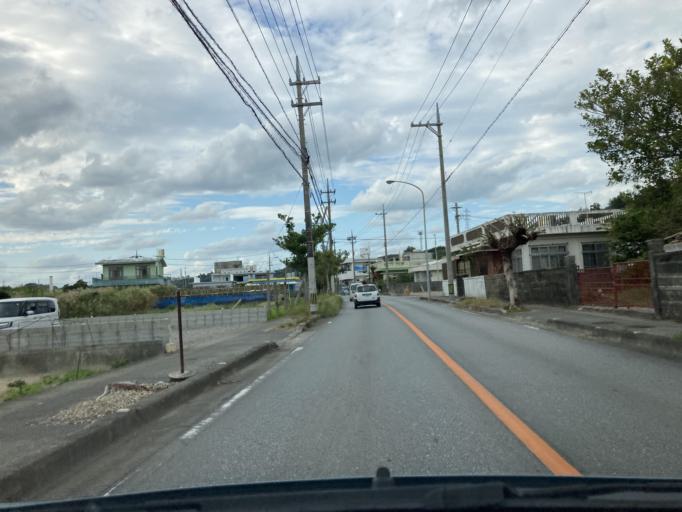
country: JP
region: Okinawa
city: Katsuren-haebaru
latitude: 26.3391
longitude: 127.8725
